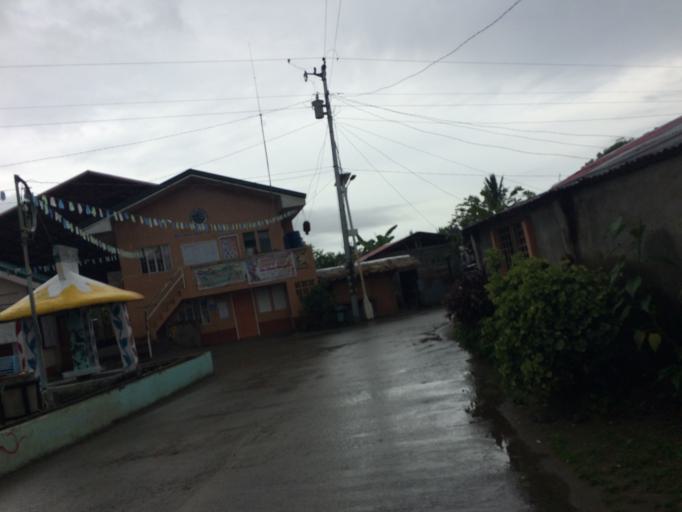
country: PH
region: Eastern Visayas
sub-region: Province of Leyte
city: Bugho
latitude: 10.8063
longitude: 124.9690
